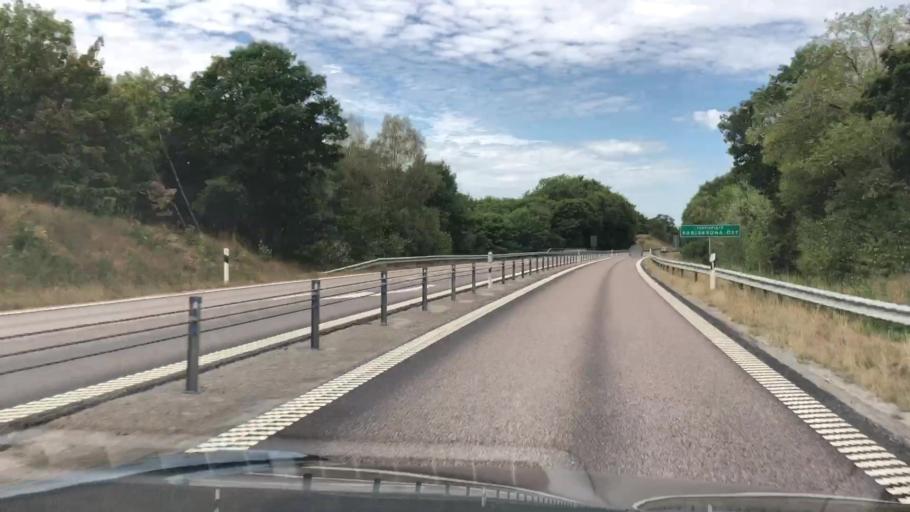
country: SE
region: Blekinge
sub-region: Karlskrona Kommun
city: Rodeby
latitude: 56.2031
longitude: 15.6584
